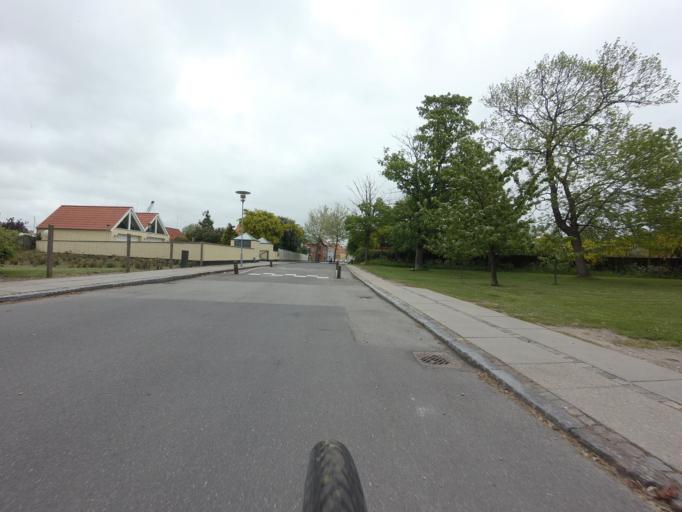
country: DK
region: Zealand
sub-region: Slagelse Kommune
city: Skaelskor
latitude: 55.2510
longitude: 11.2905
